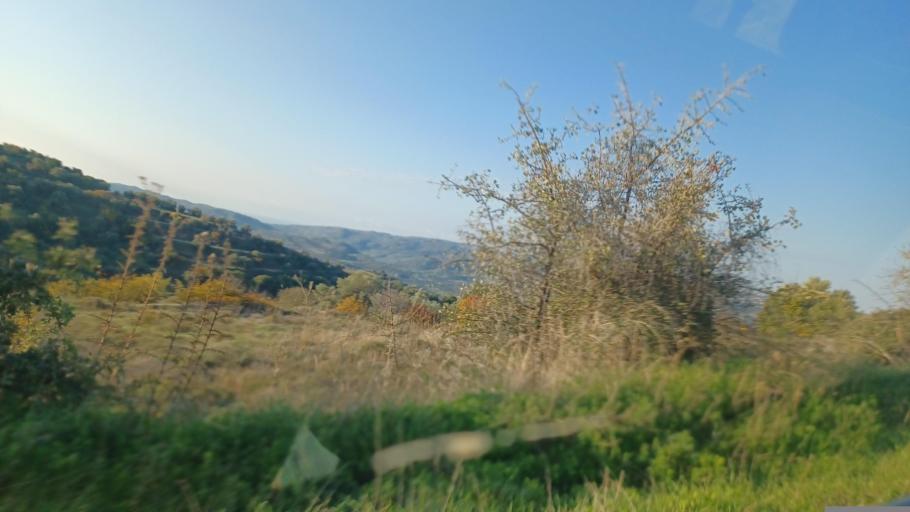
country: CY
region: Pafos
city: Mesogi
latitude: 34.8707
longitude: 32.5798
